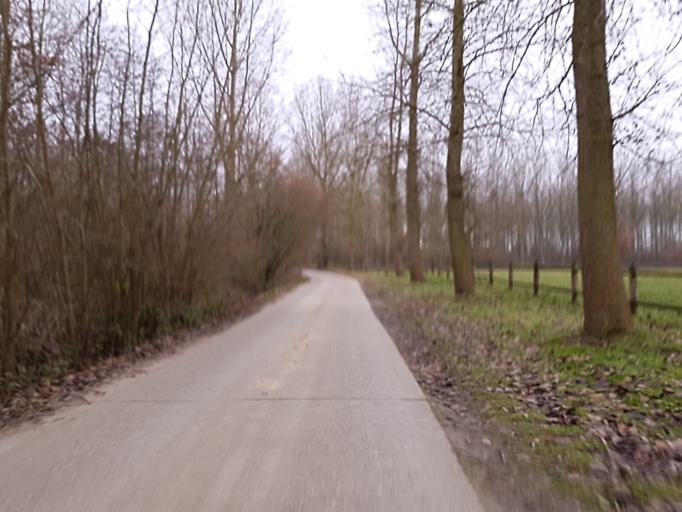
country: BE
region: Flanders
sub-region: Provincie Antwerpen
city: Rumst
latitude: 51.0409
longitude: 4.4228
